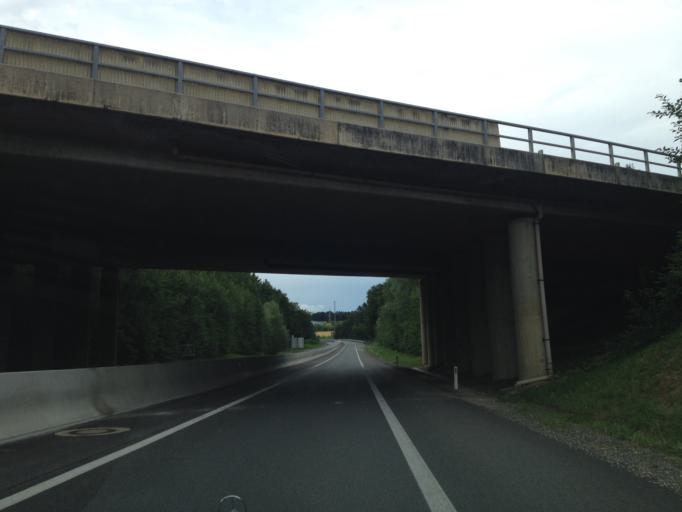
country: AT
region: Styria
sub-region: Politischer Bezirk Hartberg-Fuerstenfeld
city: Sankt Johann in der Haide
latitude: 47.2738
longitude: 16.0102
